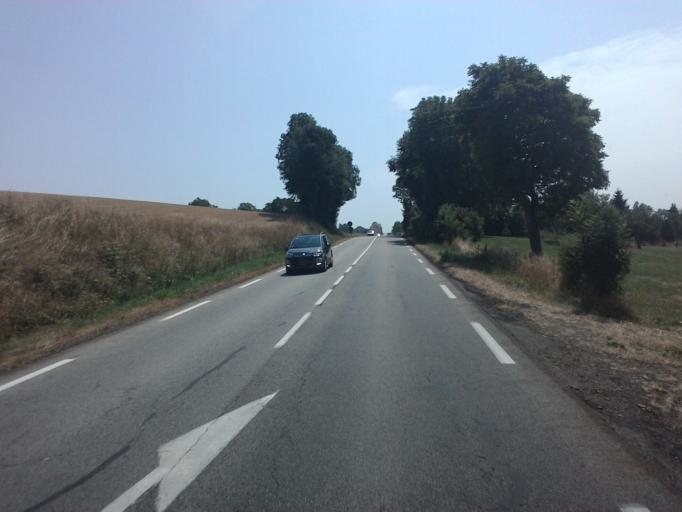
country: FR
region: Rhone-Alpes
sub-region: Departement de l'Isere
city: Montferrat
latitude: 45.4703
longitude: 5.5827
